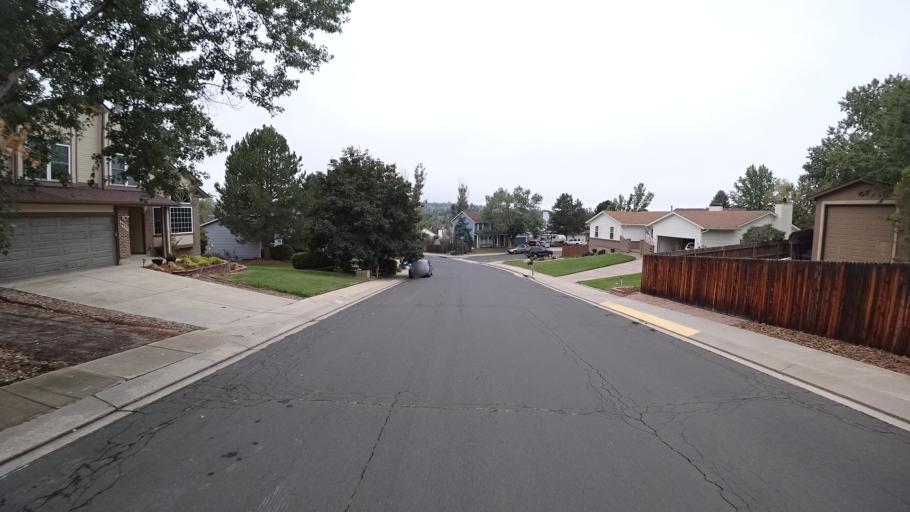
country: US
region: Colorado
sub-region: El Paso County
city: Cimarron Hills
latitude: 38.9336
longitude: -104.7620
